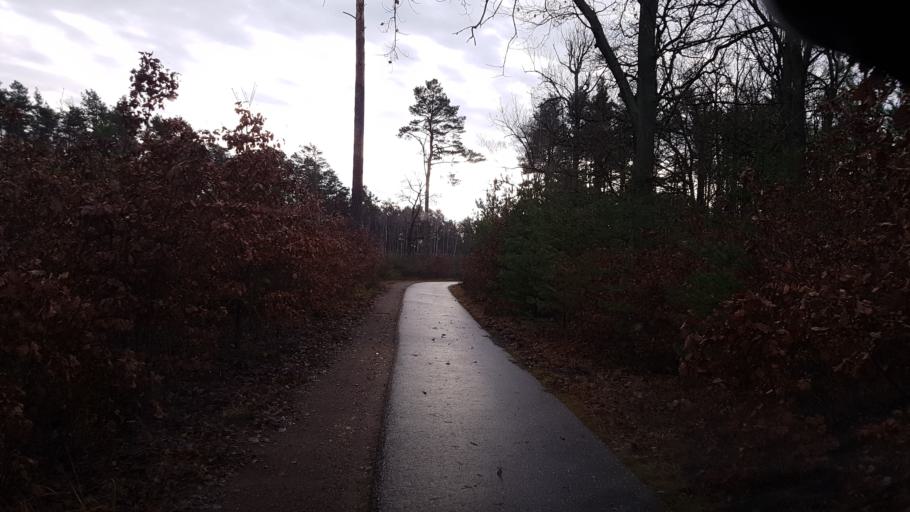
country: DE
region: Brandenburg
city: Lebusa
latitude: 51.7700
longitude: 13.4267
